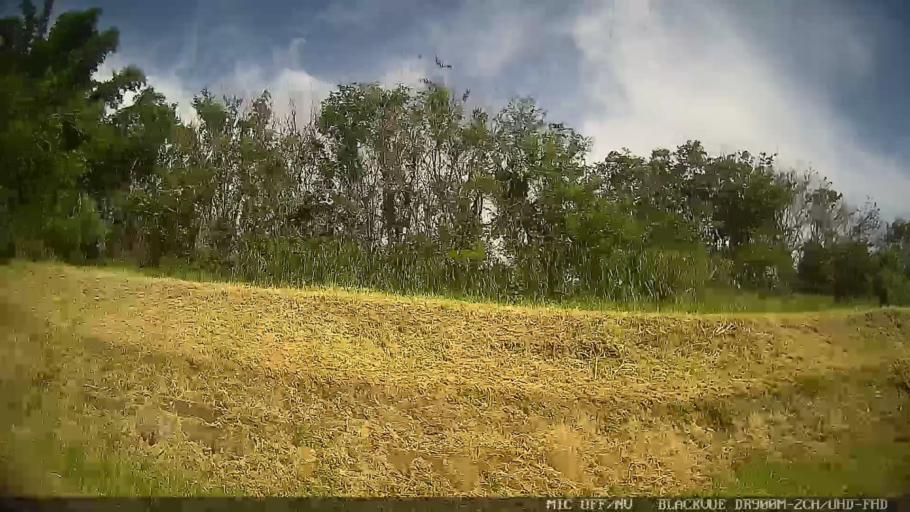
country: BR
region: Sao Paulo
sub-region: Tiete
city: Tiete
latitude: -23.1084
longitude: -47.6951
